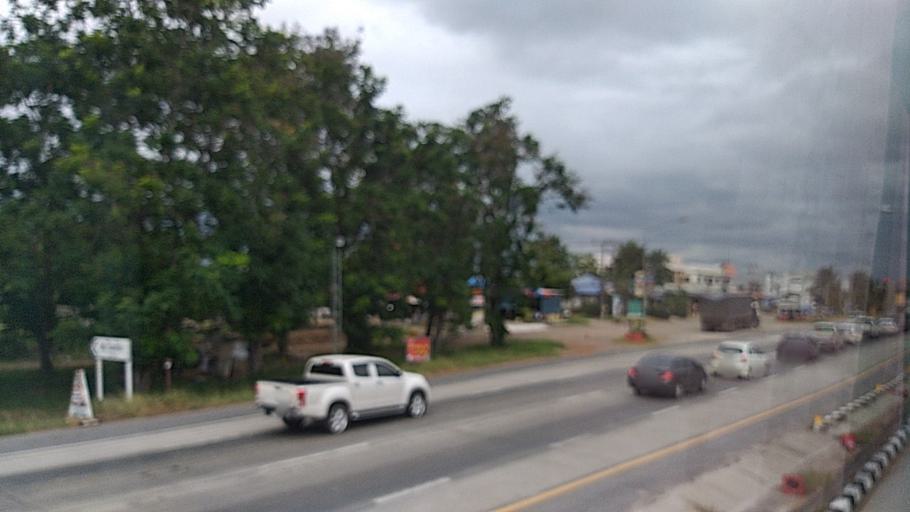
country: TH
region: Khon Kaen
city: Non Sila
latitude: 15.9651
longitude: 102.6911
